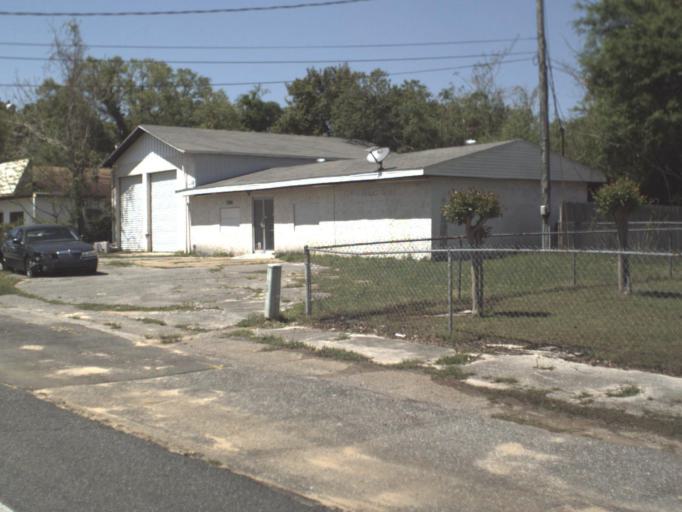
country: US
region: Florida
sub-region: Escambia County
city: Bellview
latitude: 30.4956
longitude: -87.3290
